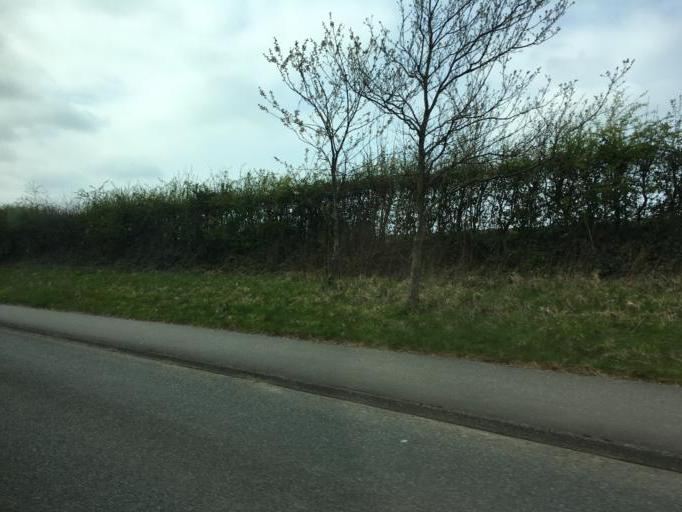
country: GB
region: Wales
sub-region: Gwynedd
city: Y Felinheli
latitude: 53.1696
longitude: -4.2349
